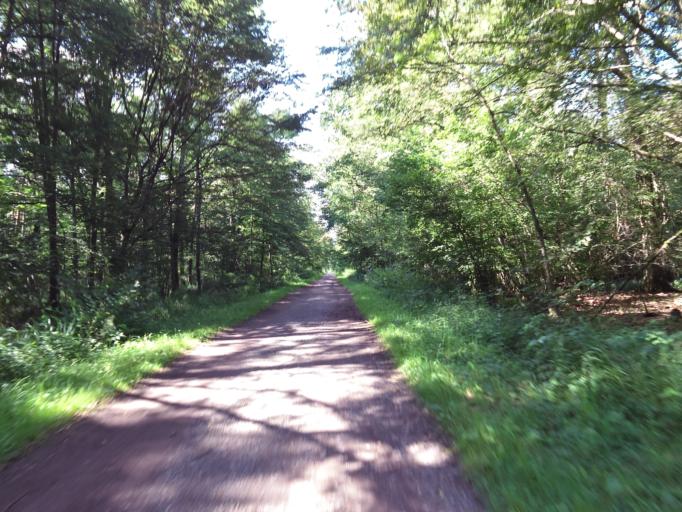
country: DE
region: Rheinland-Pfalz
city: Hanhofen
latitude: 49.3374
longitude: 8.3332
